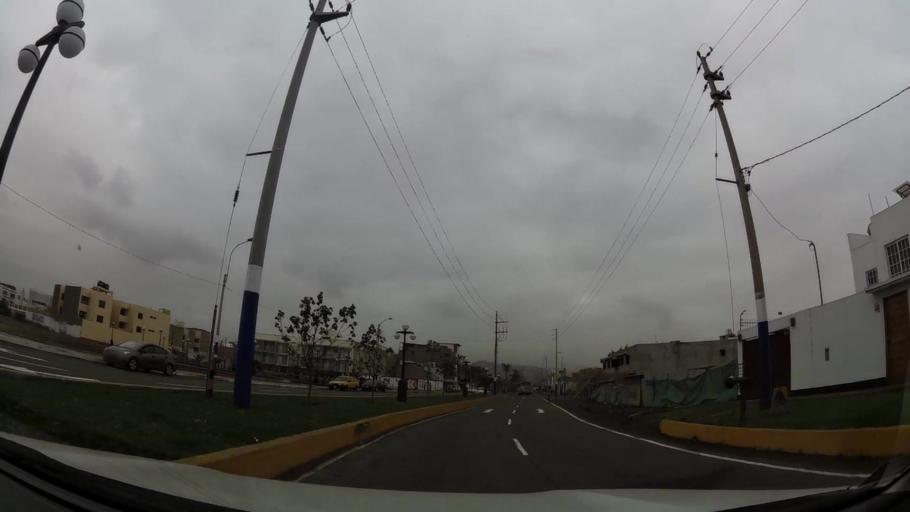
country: PE
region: Lima
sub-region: Lima
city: Surco
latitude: -12.2058
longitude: -77.0104
